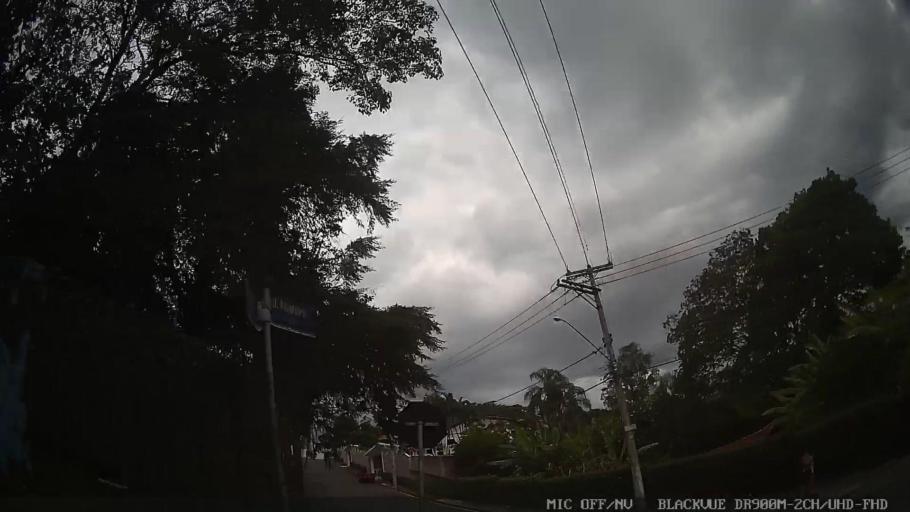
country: BR
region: Sao Paulo
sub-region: Amparo
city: Amparo
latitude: -22.7018
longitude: -46.7488
